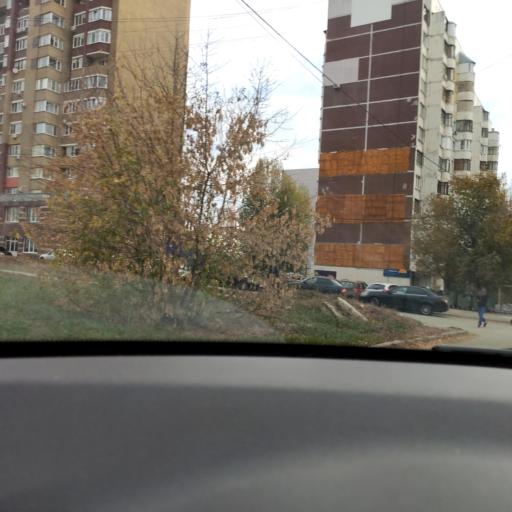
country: RU
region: Samara
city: Samara
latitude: 53.2107
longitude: 50.2134
